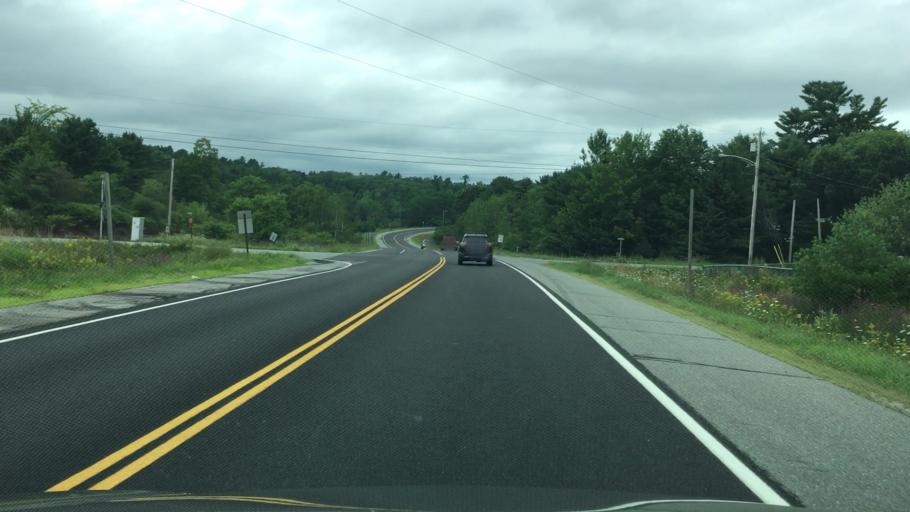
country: US
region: Maine
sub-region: Penobscot County
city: Orrington
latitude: 44.6955
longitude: -68.8151
